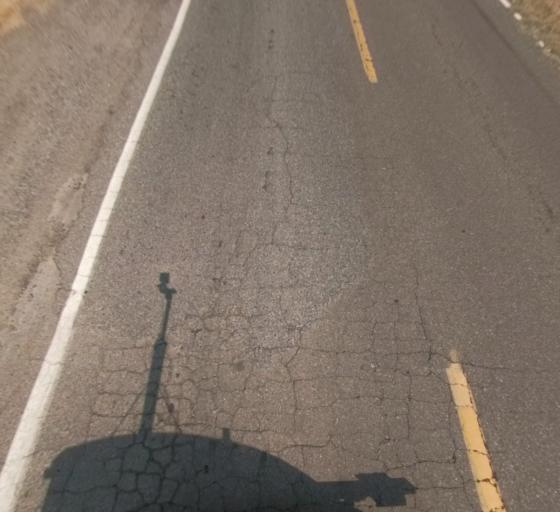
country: US
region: California
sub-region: Madera County
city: Fairmead
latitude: 37.1424
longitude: -120.1616
